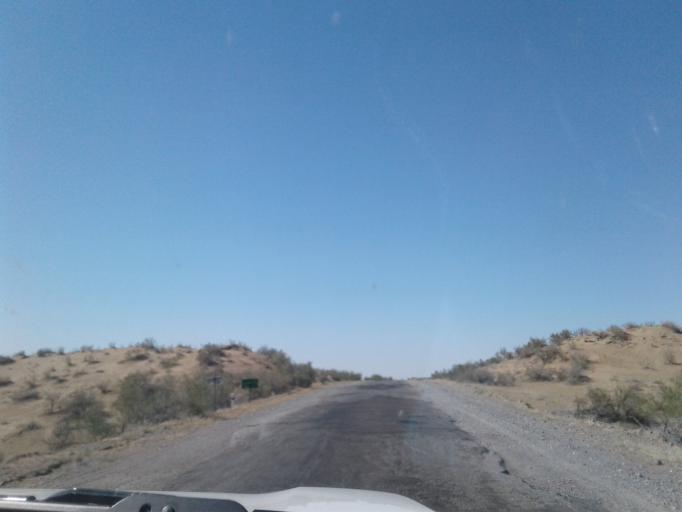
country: AF
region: Badghis
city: Bala Murghab
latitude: 36.1963
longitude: 62.6025
